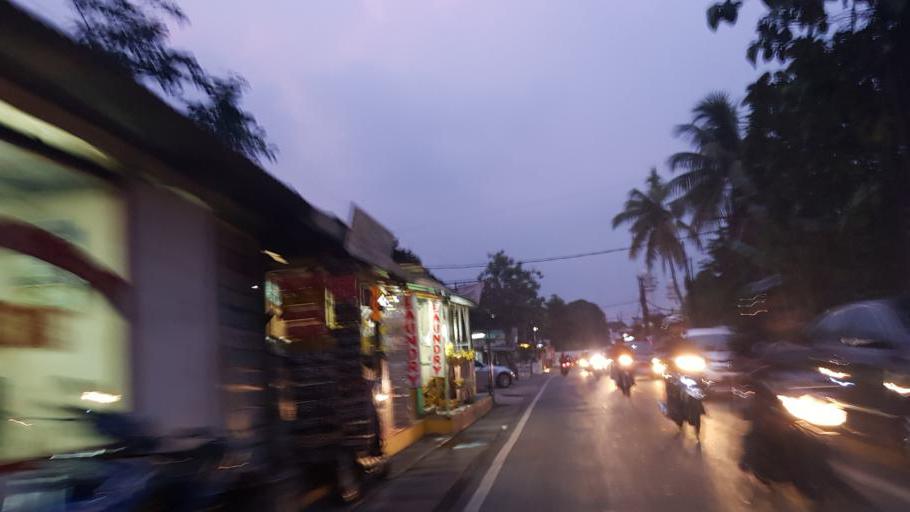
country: ID
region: West Java
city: Depok
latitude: -6.3473
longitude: 106.8026
